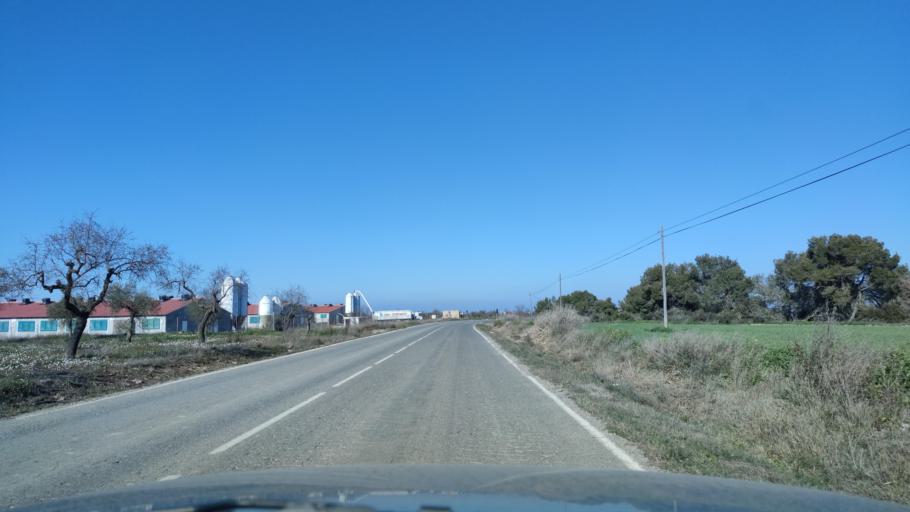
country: ES
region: Catalonia
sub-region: Provincia de Lleida
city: Maials
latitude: 41.3159
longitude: 0.4269
